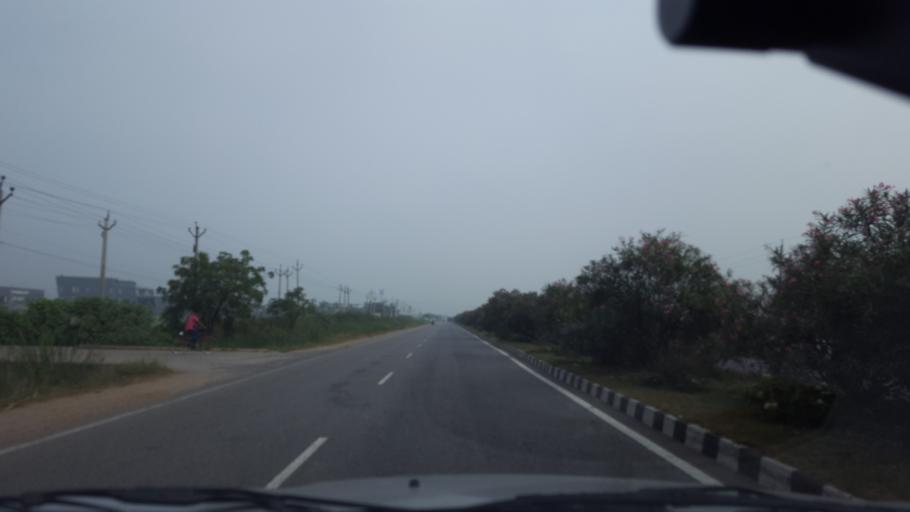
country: IN
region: Andhra Pradesh
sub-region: Guntur
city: Chilakalurupet
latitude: 16.0618
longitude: 80.1492
